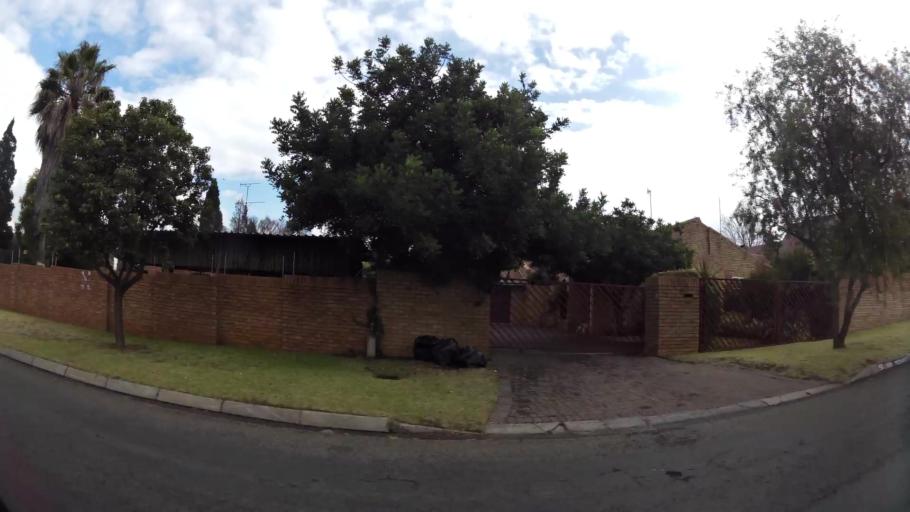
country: ZA
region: Gauteng
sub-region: Sedibeng District Municipality
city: Vanderbijlpark
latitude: -26.7395
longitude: 27.8548
